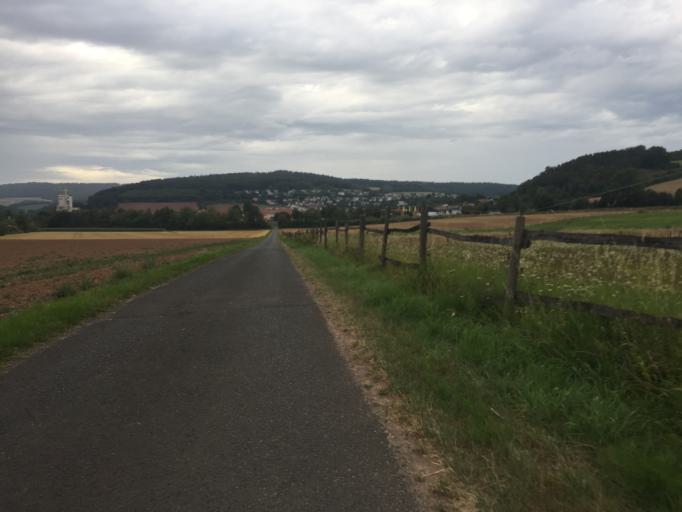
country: DE
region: Hesse
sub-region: Regierungsbezirk Kassel
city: Alheim
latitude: 51.0599
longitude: 9.6229
